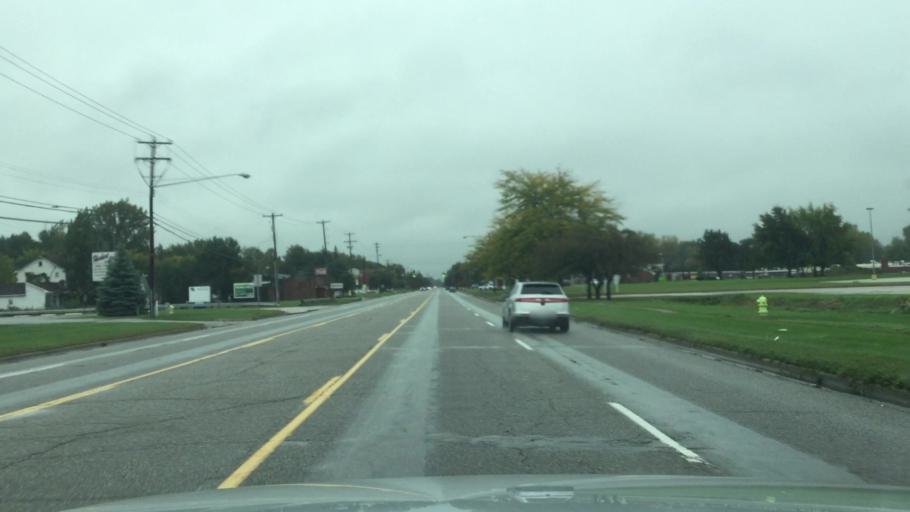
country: US
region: Michigan
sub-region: Saginaw County
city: Bridgeport
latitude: 43.3817
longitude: -83.8984
